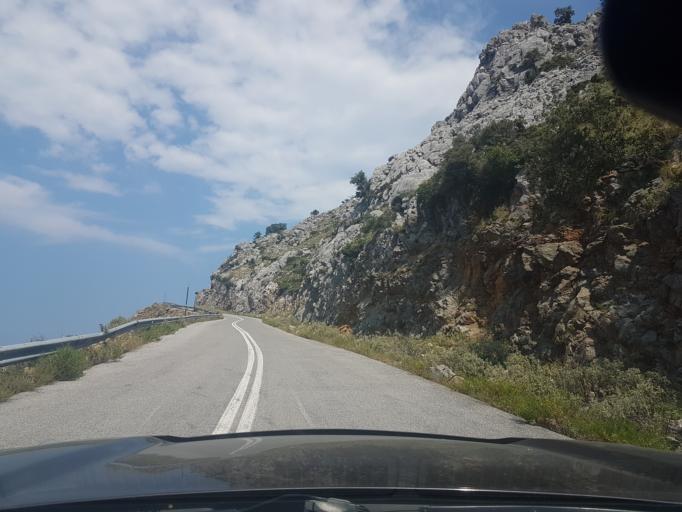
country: GR
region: Central Greece
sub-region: Nomos Evvoias
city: Kymi
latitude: 38.6556
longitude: 23.9658
